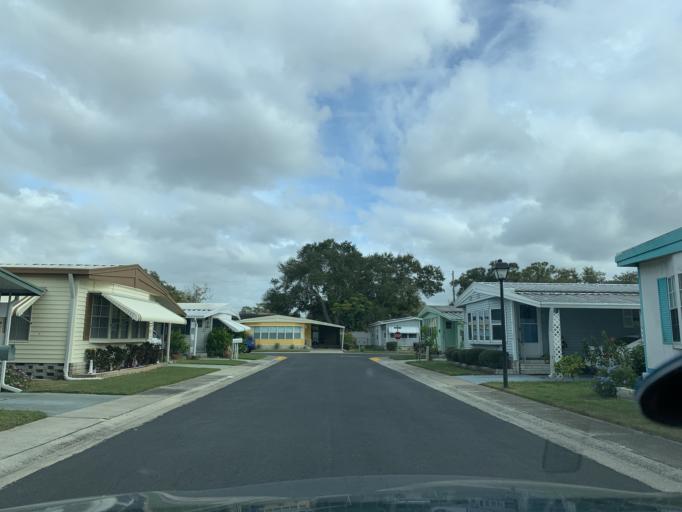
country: US
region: Florida
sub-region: Pinellas County
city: Ridgecrest
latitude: 27.8830
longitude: -82.7890
